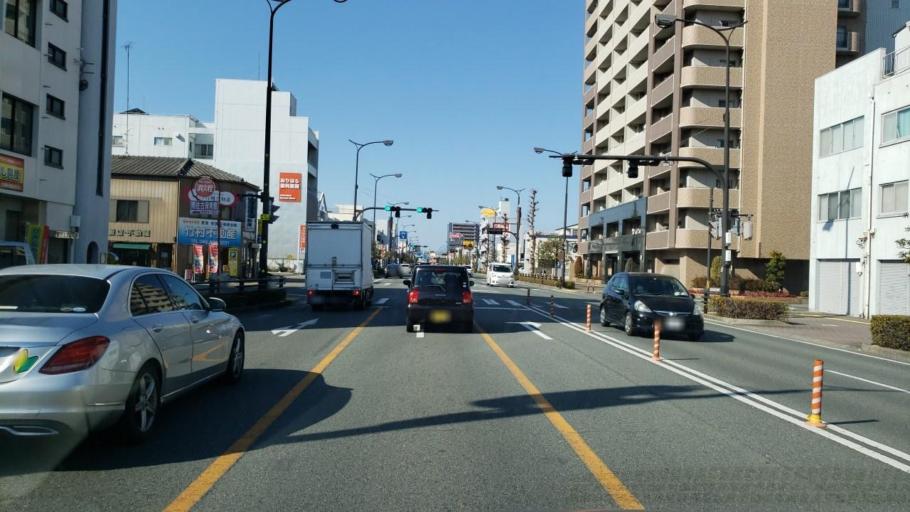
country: JP
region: Tokushima
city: Tokushima-shi
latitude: 34.0782
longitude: 134.5350
